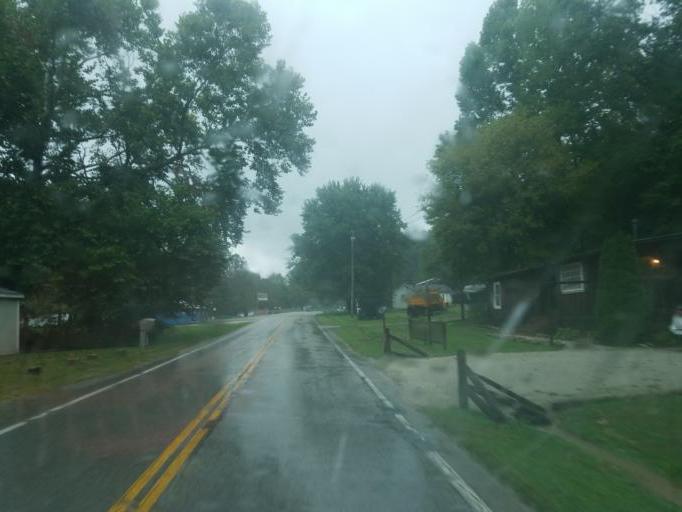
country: US
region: Kentucky
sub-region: Rowan County
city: Morehead
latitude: 38.2545
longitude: -83.3367
